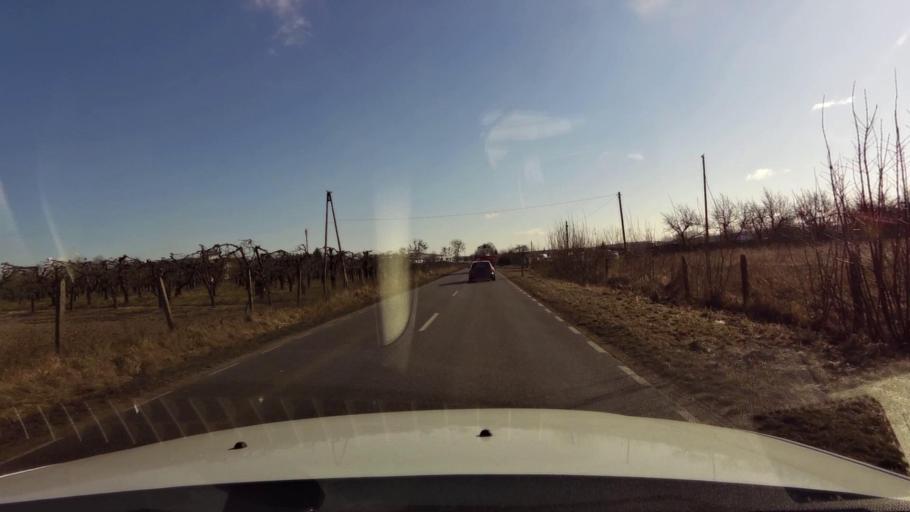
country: PL
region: West Pomeranian Voivodeship
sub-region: Powiat mysliborski
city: Barlinek
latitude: 52.9928
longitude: 15.1866
